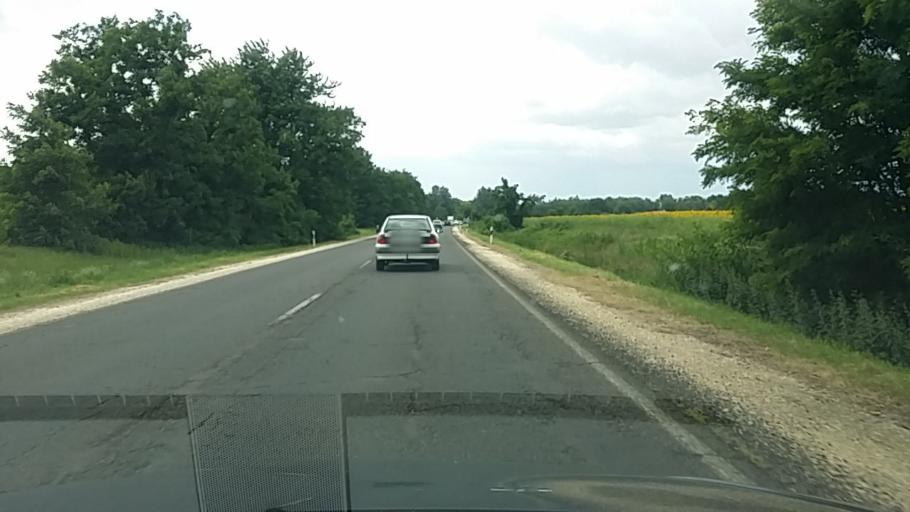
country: HU
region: Pest
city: Orkeny
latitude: 47.1453
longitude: 19.3961
